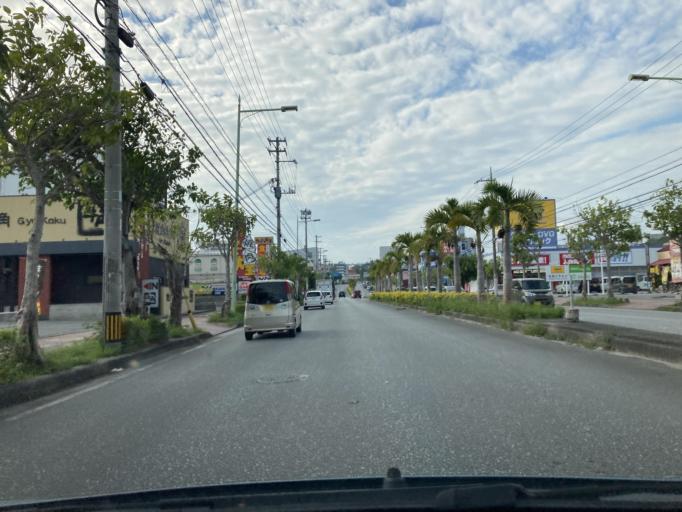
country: JP
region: Okinawa
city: Okinawa
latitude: 26.3175
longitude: 127.8244
